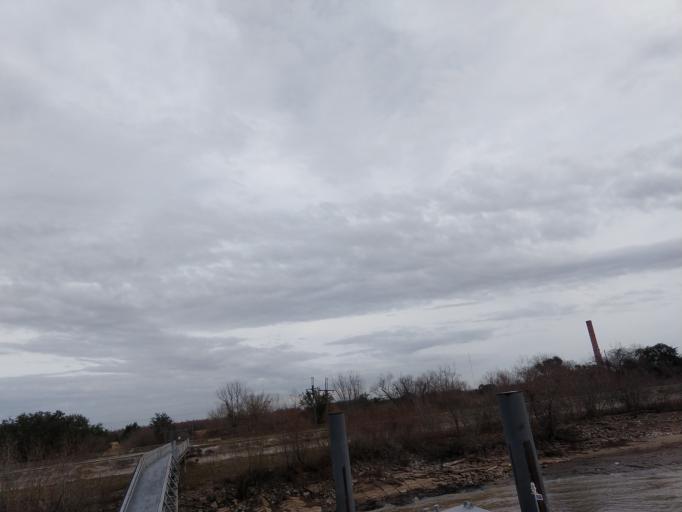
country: US
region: Louisiana
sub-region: Saint Bernard Parish
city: Arabi
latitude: 29.9392
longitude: -89.9944
